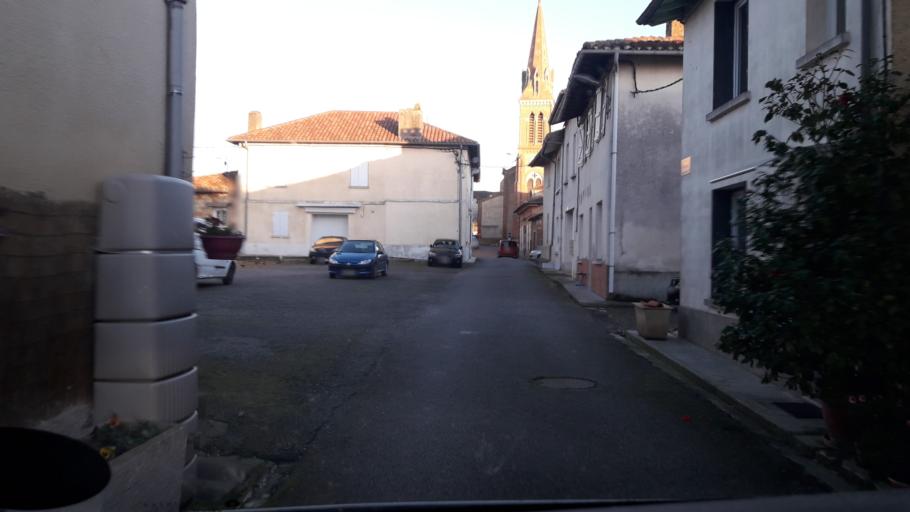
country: FR
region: Midi-Pyrenees
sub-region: Departement du Gers
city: Gimont
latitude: 43.5982
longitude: 0.9792
